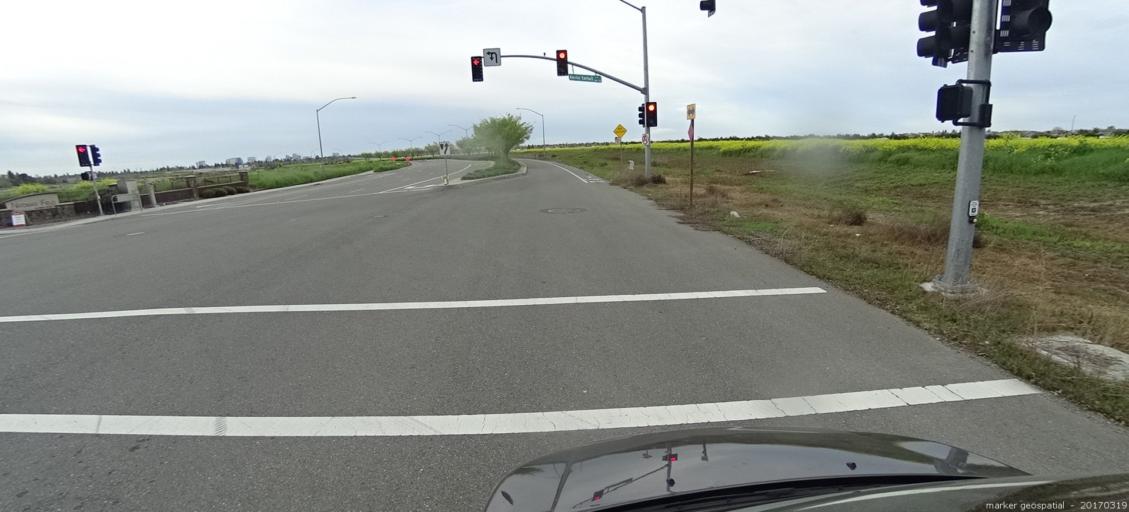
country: US
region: California
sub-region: Yolo County
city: West Sacramento
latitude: 38.6398
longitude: -121.5199
